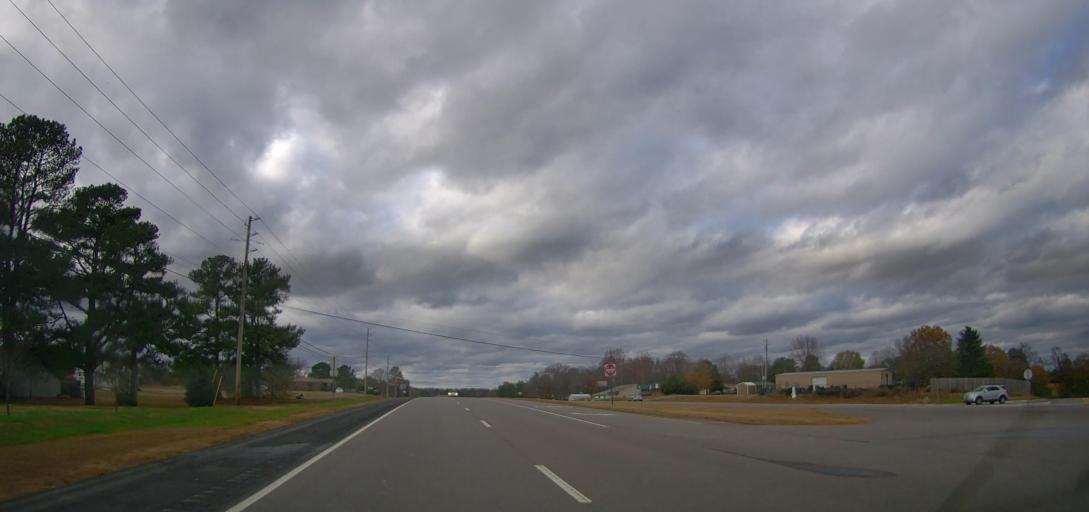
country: US
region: Alabama
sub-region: Morgan County
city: Falkville
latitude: 34.2513
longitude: -86.9701
